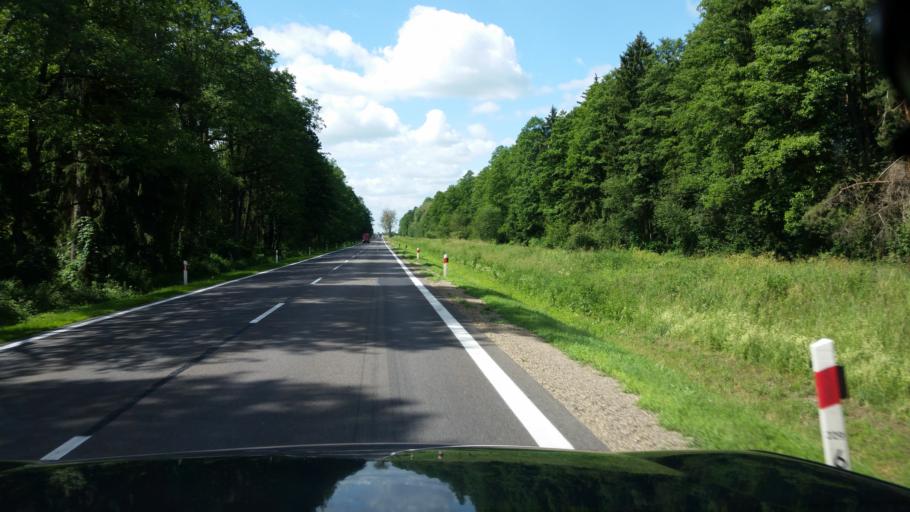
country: PL
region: Podlasie
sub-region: Powiat grajewski
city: Rajgrod
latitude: 53.6921
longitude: 22.6372
